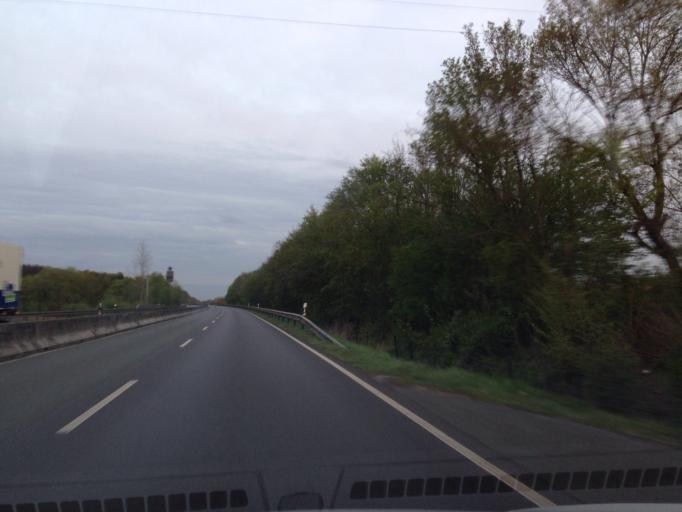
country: DE
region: North Rhine-Westphalia
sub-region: Regierungsbezirk Munster
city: Altenberge
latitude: 52.0104
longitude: 7.5042
